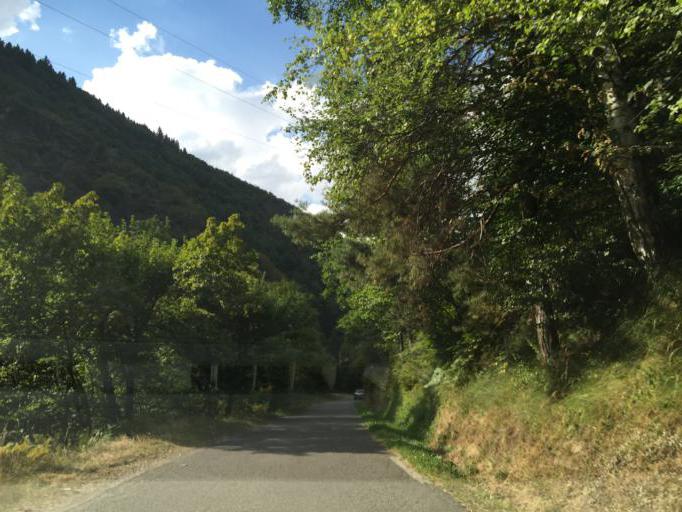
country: FR
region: Rhone-Alpes
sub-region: Departement de la Loire
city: Saint-Jean-Bonnefonds
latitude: 45.3966
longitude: 4.4478
